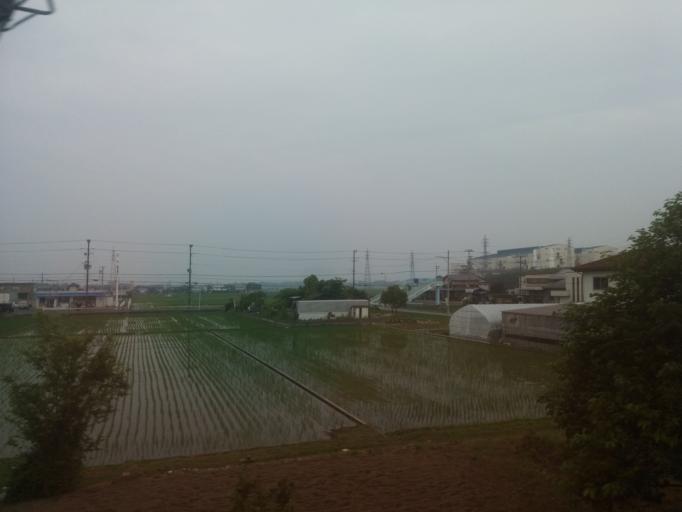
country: JP
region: Shiga Prefecture
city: Youkaichi
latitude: 35.1876
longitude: 136.1745
